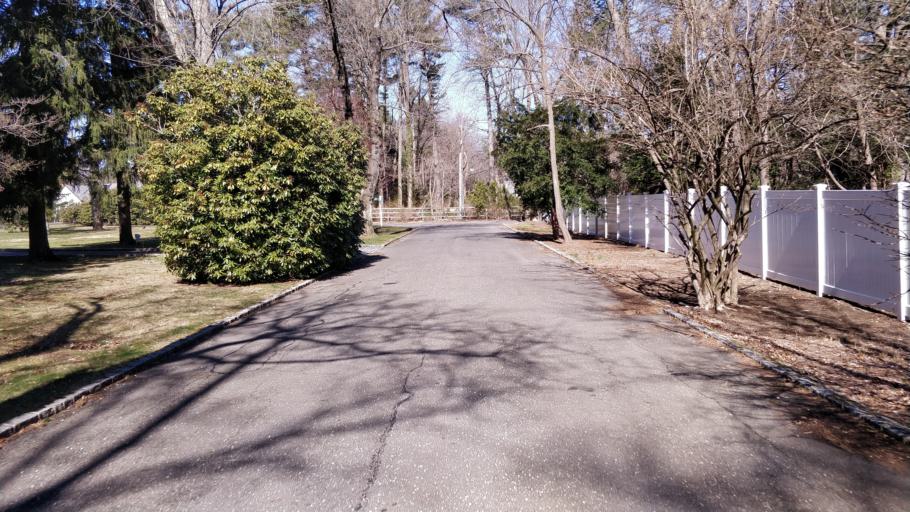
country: US
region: New York
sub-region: Nassau County
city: Syosset
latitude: 40.8318
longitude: -73.5101
